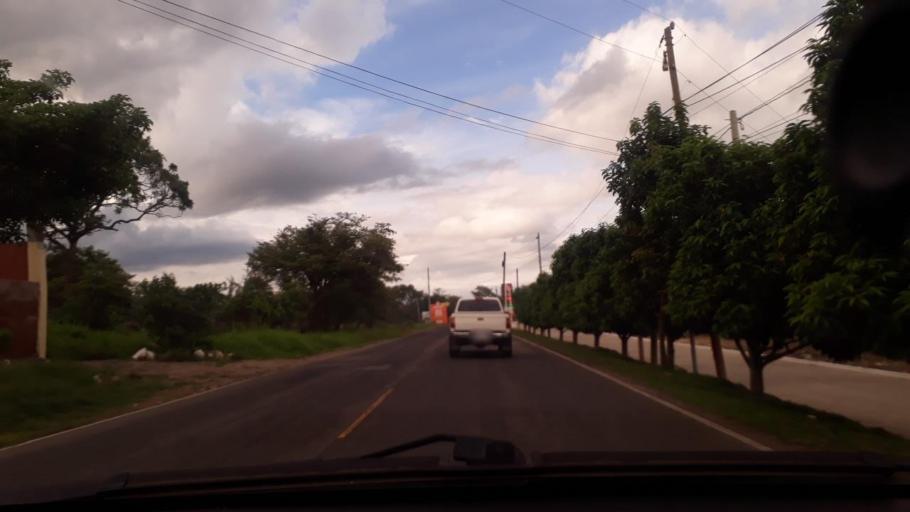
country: GT
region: Jutiapa
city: Jutiapa
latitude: 14.2811
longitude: -89.9565
